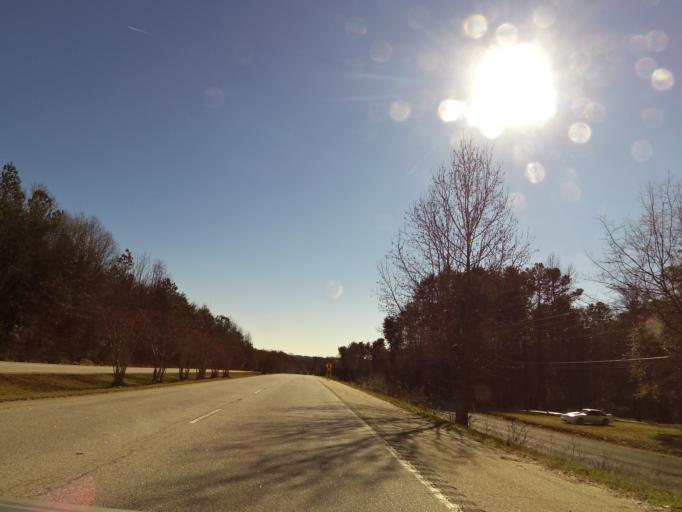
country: US
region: South Carolina
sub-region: Greenville County
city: Travelers Rest
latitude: 34.9415
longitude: -82.4355
